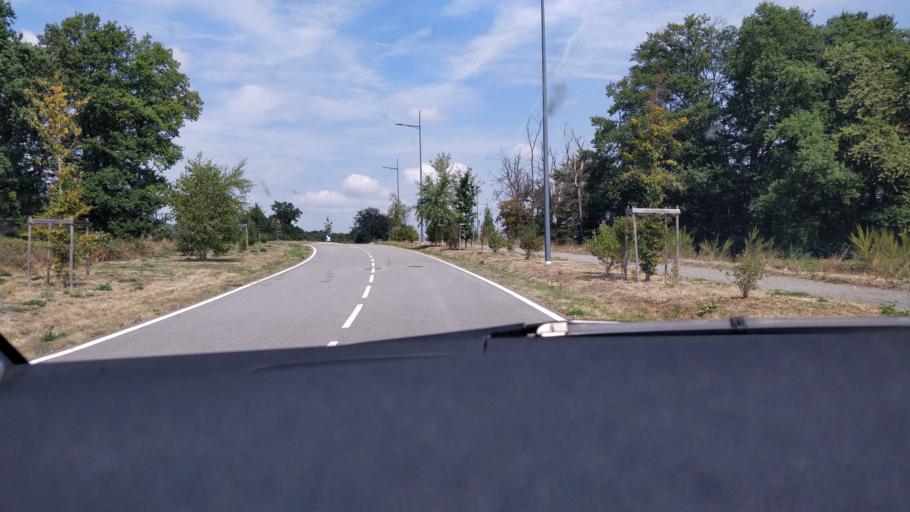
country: FR
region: Limousin
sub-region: Departement de la Haute-Vienne
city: Le Palais-sur-Vienne
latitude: 45.8623
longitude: 1.2996
